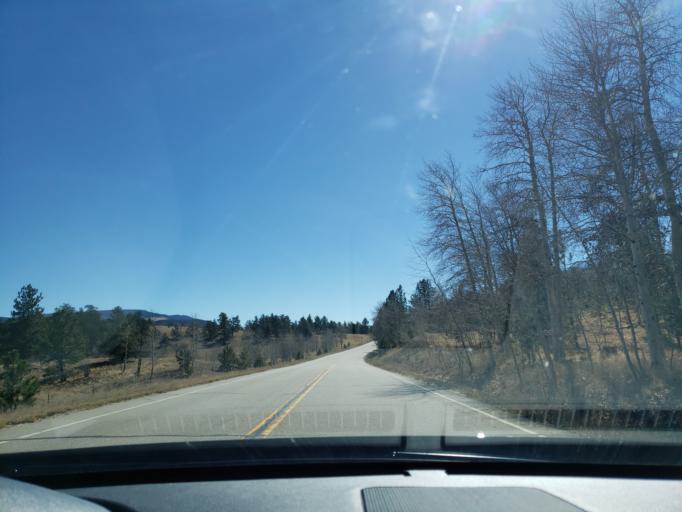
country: US
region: Colorado
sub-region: Chaffee County
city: Buena Vista
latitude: 38.8863
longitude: -105.6823
